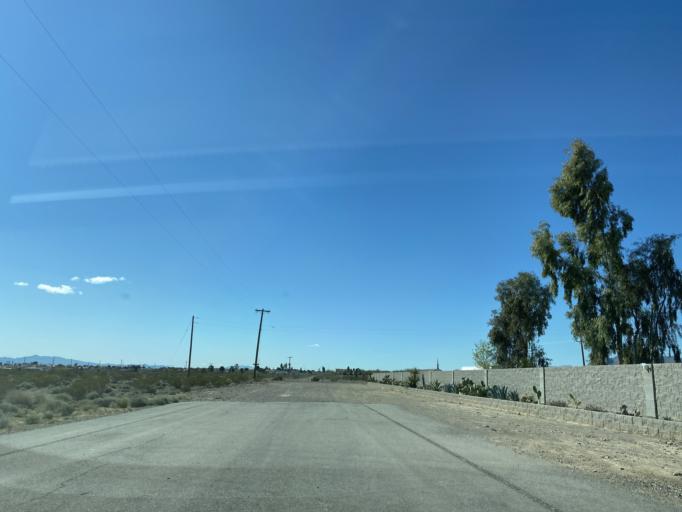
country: US
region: Nevada
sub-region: Clark County
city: North Las Vegas
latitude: 36.3259
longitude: -115.2853
